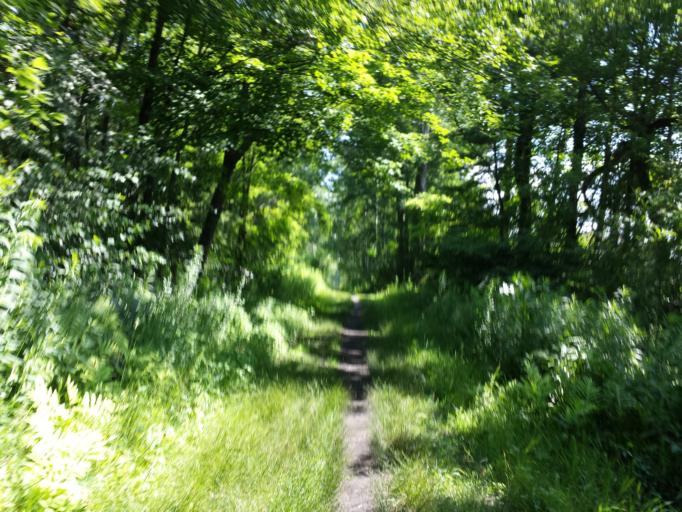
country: US
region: Vermont
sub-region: Rutland County
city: Castleton
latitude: 43.5945
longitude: -73.1929
